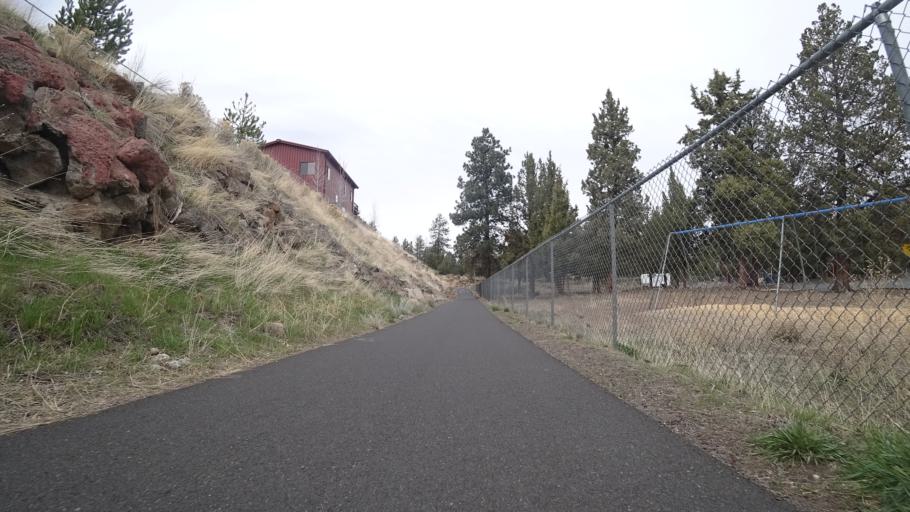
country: US
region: Oregon
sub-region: Deschutes County
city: Bend
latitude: 44.0502
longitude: -121.2887
